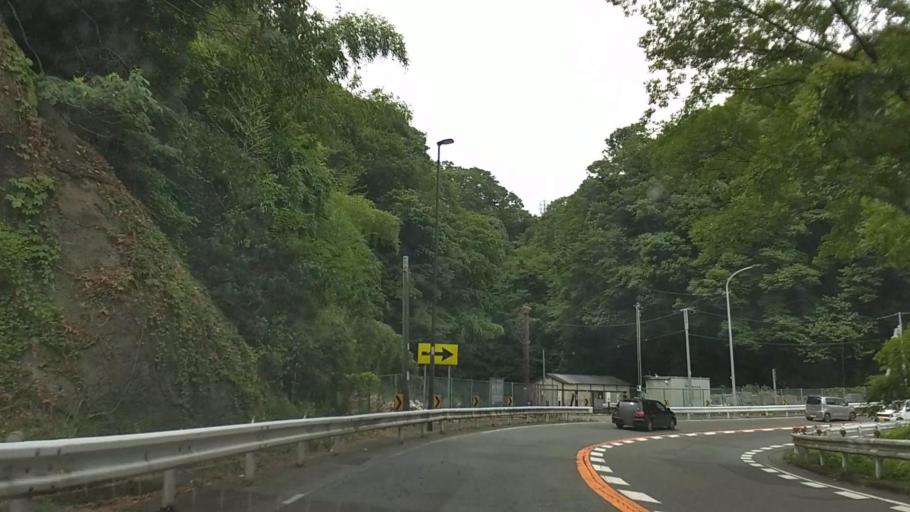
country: JP
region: Yamanashi
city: Uenohara
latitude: 35.6168
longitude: 139.1699
